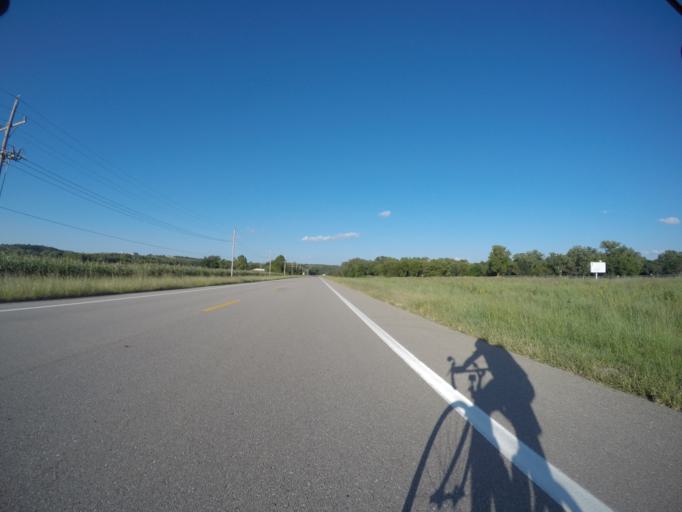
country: US
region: Kansas
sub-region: Riley County
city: Manhattan
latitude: 39.1538
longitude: -96.6382
